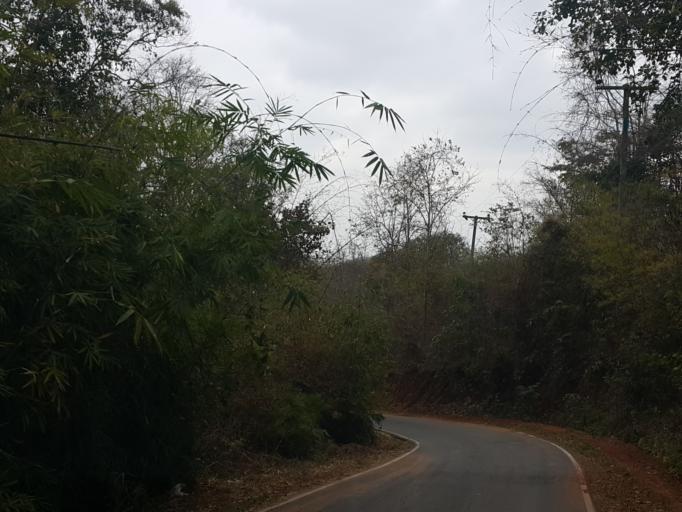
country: TH
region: Chiang Mai
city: Hang Dong
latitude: 18.7174
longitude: 98.8451
